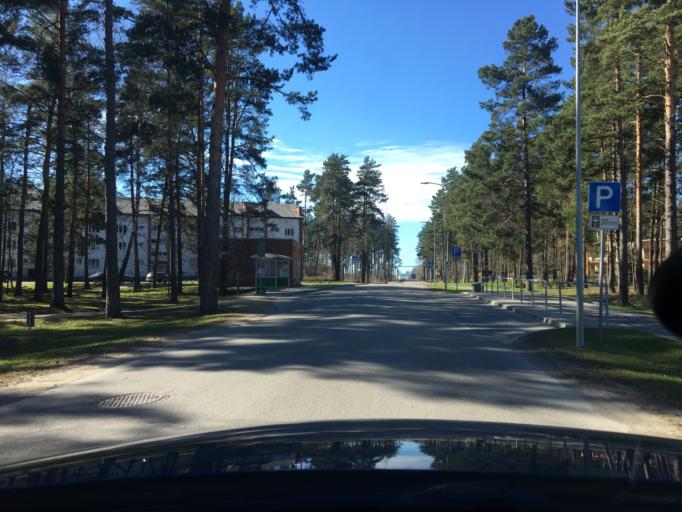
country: LV
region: Salaspils
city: Salaspils
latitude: 56.8706
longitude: 24.3449
